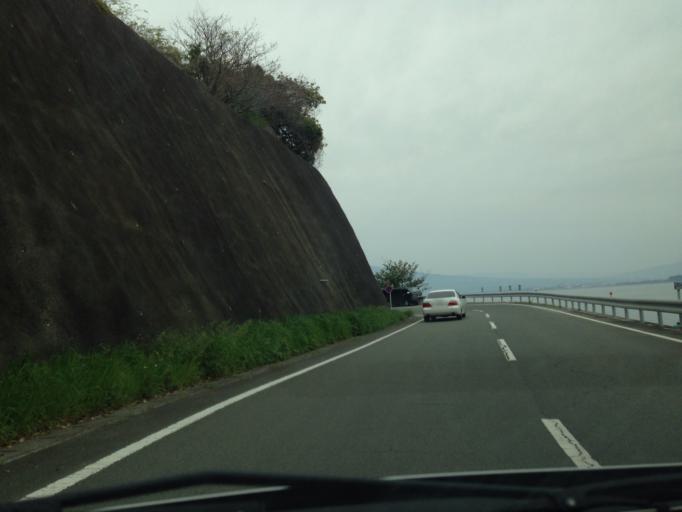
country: JP
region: Shizuoka
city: Heda
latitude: 35.0191
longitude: 138.8341
